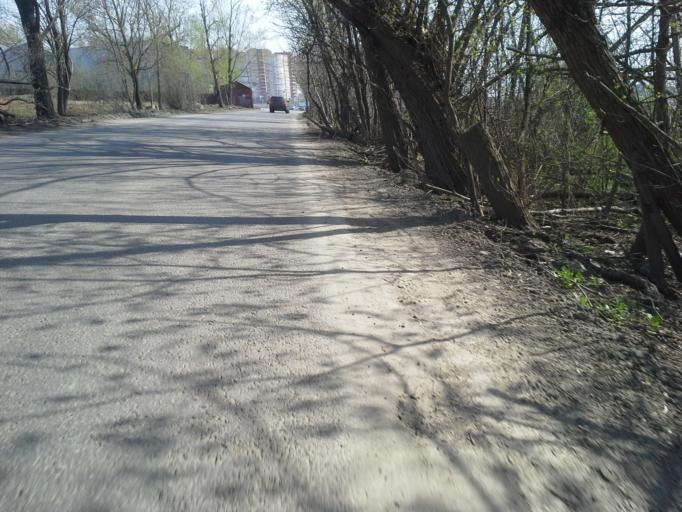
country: RU
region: Moskovskaya
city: Shcherbinka
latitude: 55.5102
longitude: 37.5505
